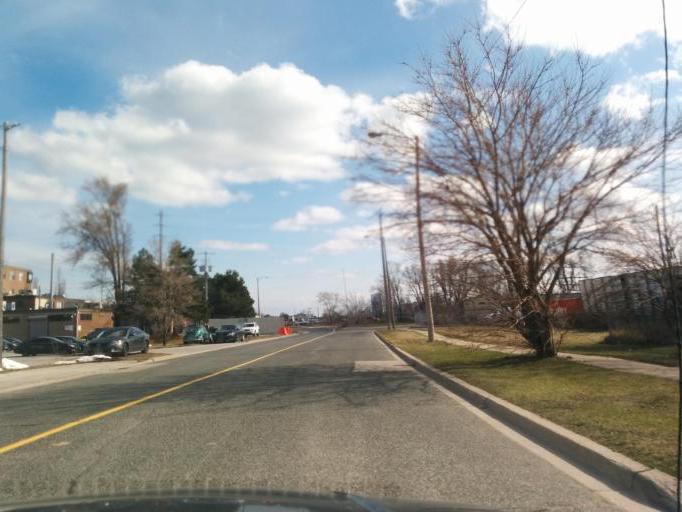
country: CA
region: Ontario
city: Etobicoke
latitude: 43.6212
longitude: -79.5186
